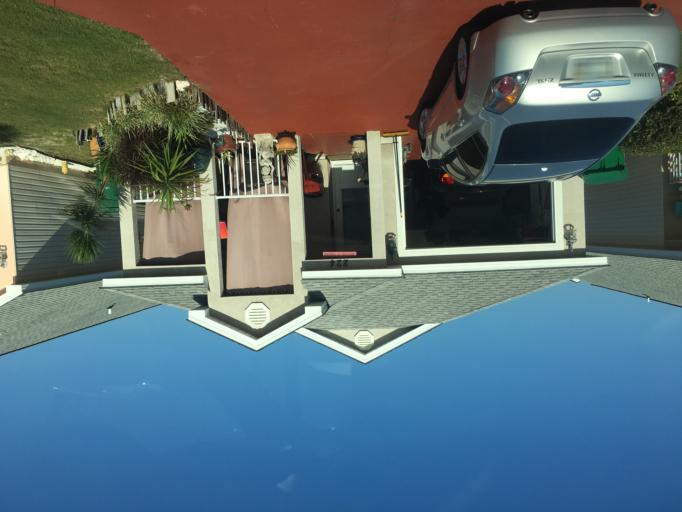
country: US
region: Florida
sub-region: Bay County
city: Panama City Beach
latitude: 30.1941
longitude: -85.8212
